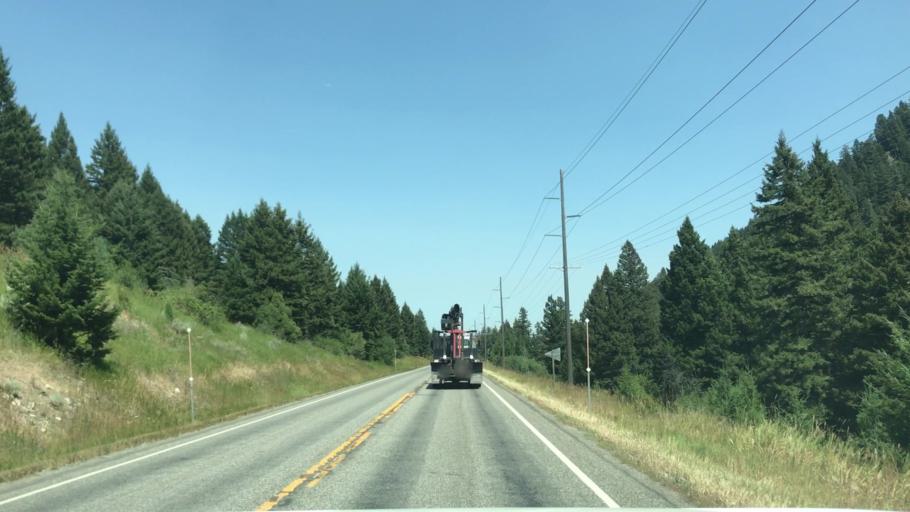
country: US
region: Montana
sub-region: Gallatin County
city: Four Corners
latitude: 45.5116
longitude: -111.2590
